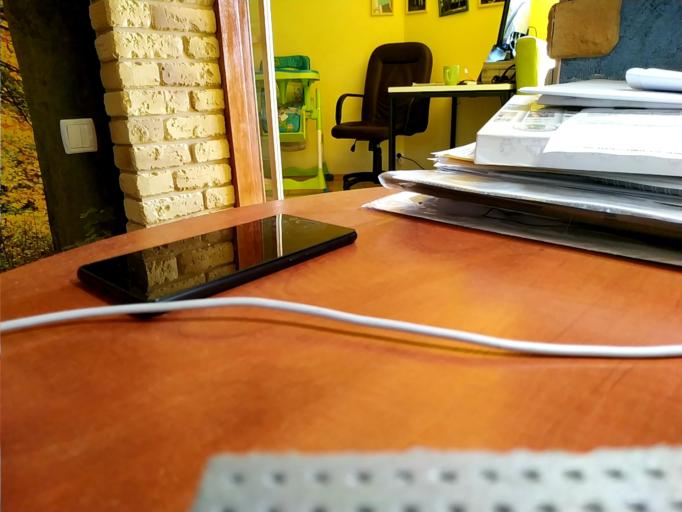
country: RU
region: Tverskaya
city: Kalashnikovo
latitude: 57.3841
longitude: 35.3309
